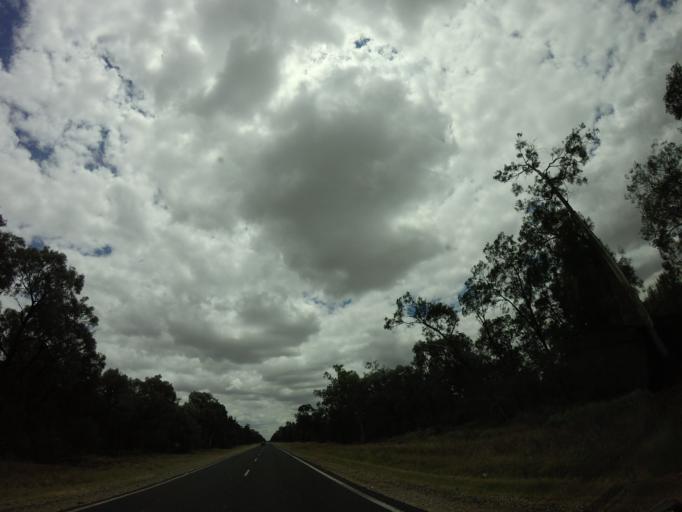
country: AU
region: Queensland
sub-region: Goondiwindi
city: Goondiwindi
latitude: -28.4206
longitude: 150.3037
